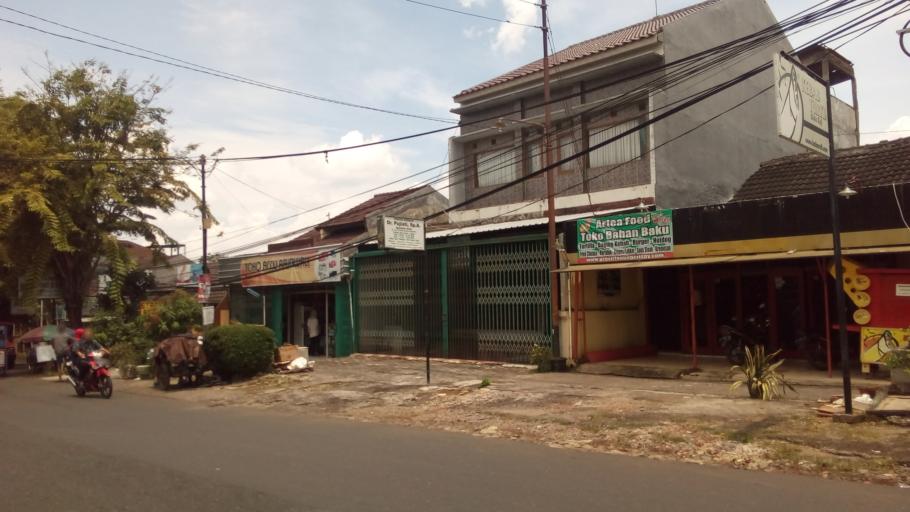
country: ID
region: Central Java
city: Ungaran
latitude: -7.0713
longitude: 110.4269
